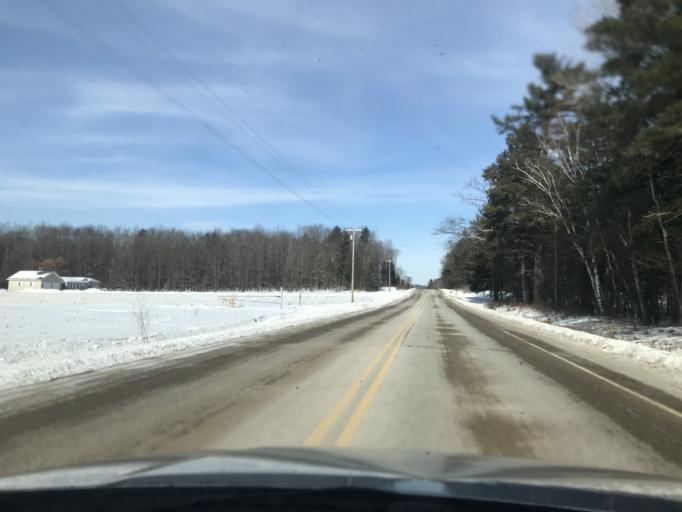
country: US
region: Wisconsin
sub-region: Oconto County
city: Oconto Falls
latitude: 45.1361
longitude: -88.1774
